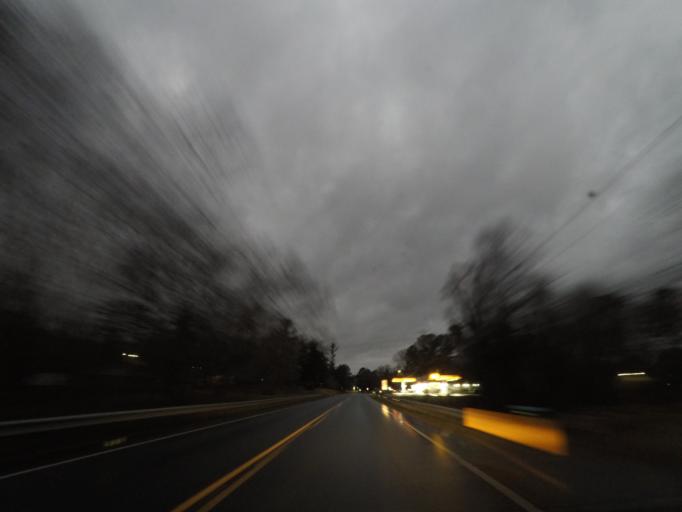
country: US
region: North Carolina
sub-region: Orange County
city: Hillsborough
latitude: 36.0782
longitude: -79.0743
